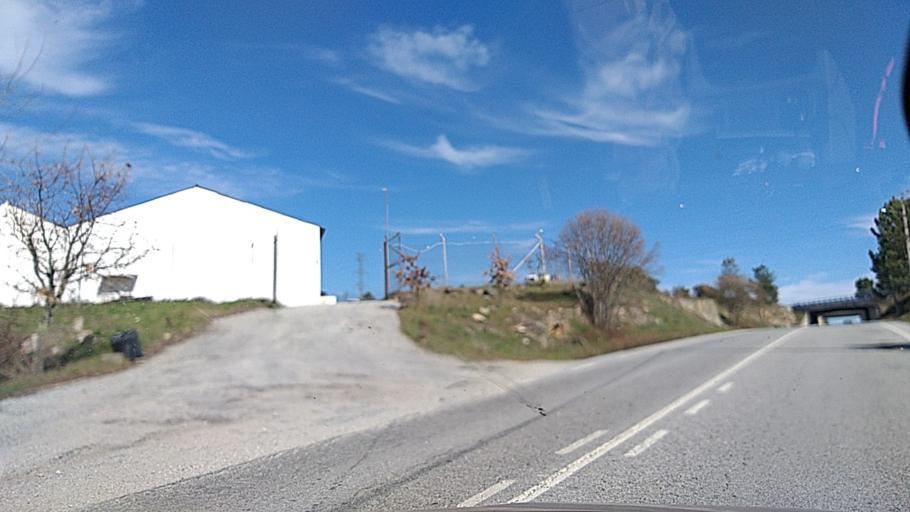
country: PT
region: Guarda
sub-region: Guarda
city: Sequeira
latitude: 40.5698
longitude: -7.2164
